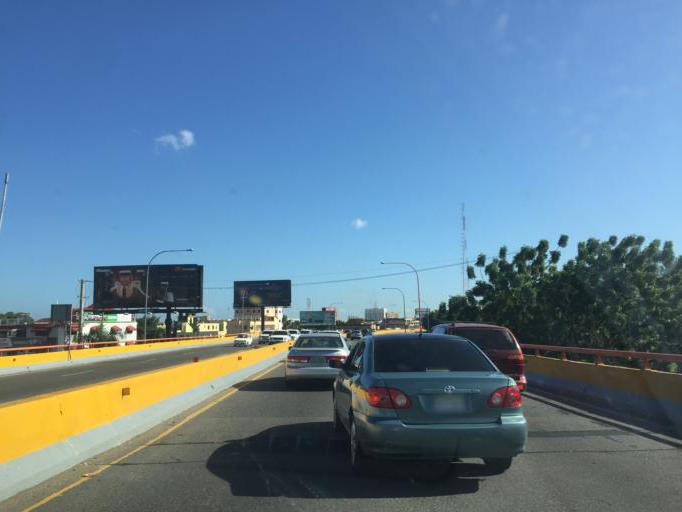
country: DO
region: Nacional
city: San Carlos
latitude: 18.4777
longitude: -69.9031
